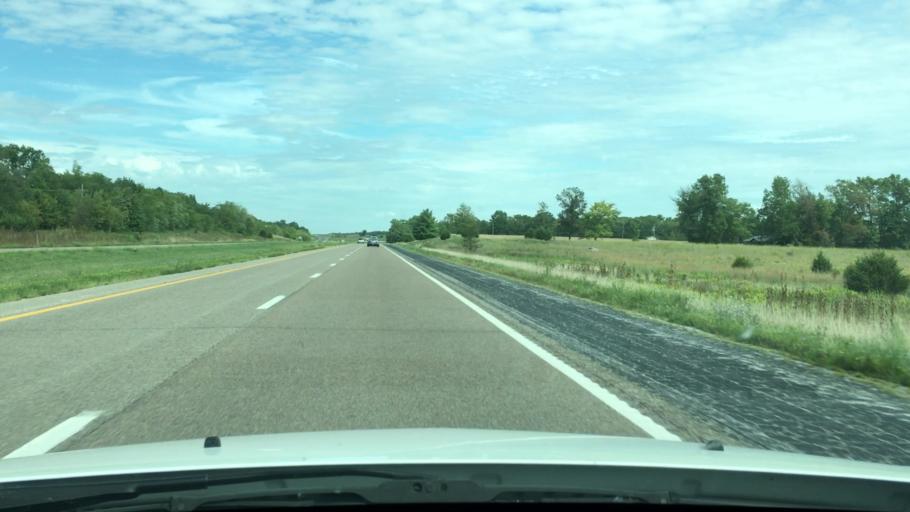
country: US
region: Missouri
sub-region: Audrain County
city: Mexico
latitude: 39.0523
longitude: -91.8940
